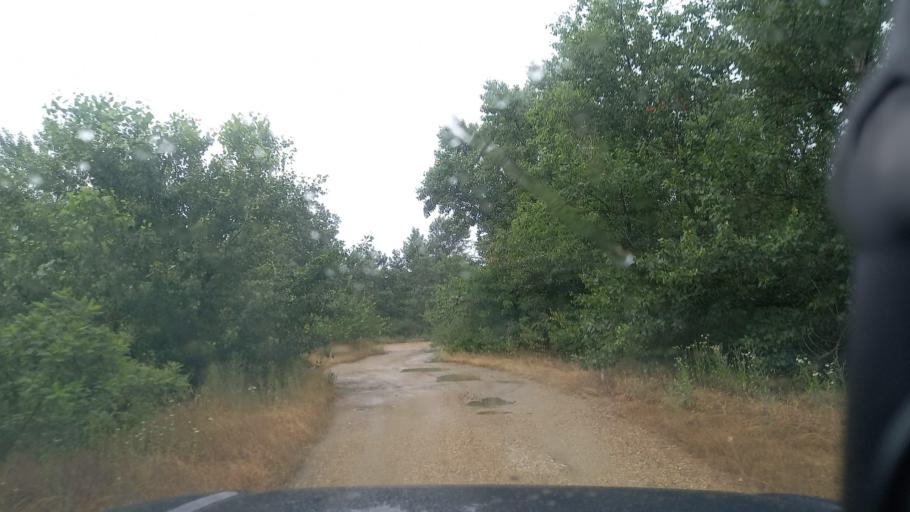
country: RU
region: Krasnodarskiy
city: Vasyurinskaya
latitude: 45.0347
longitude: 39.4705
